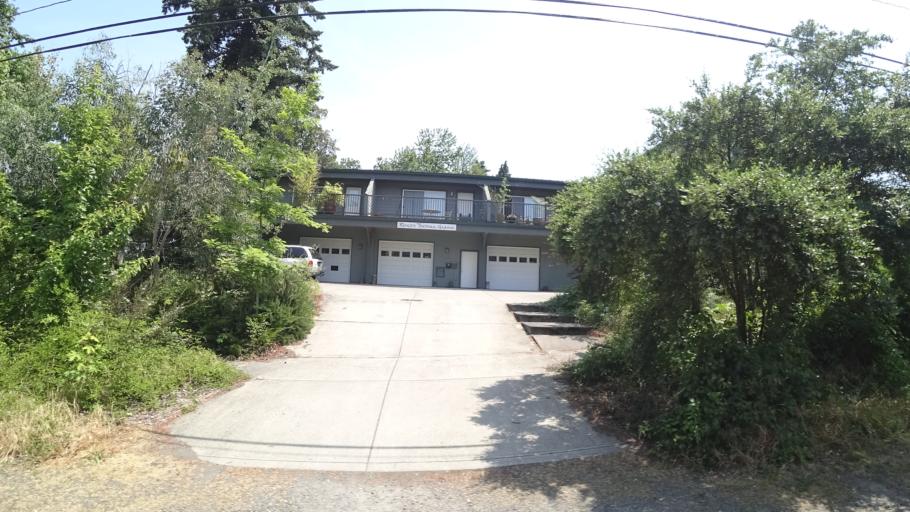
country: US
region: Oregon
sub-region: Multnomah County
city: Portland
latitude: 45.5818
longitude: -122.6763
